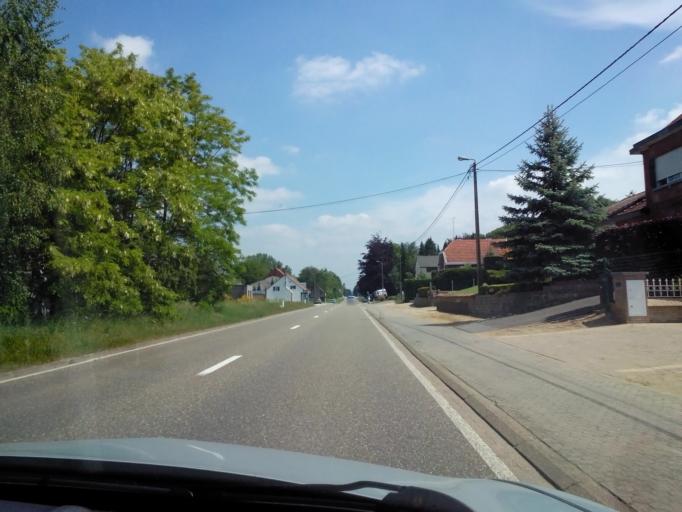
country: BE
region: Flanders
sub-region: Provincie Vlaams-Brabant
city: Aarschot
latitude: 50.9711
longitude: 4.7986
